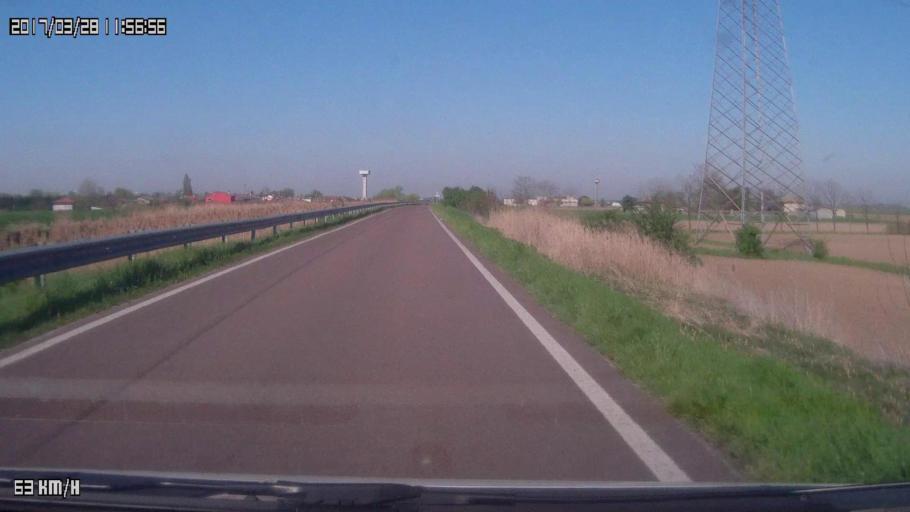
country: IT
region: Veneto
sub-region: Provincia di Venezia
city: Boscochiaro
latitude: 45.1349
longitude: 12.1321
